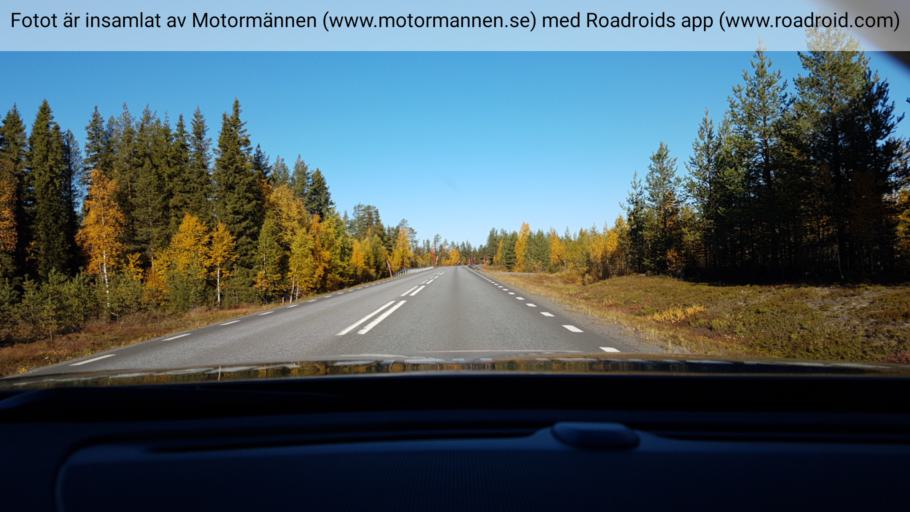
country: SE
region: Norrbotten
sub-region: Arvidsjaurs Kommun
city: Arvidsjaur
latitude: 65.4611
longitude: 19.3711
